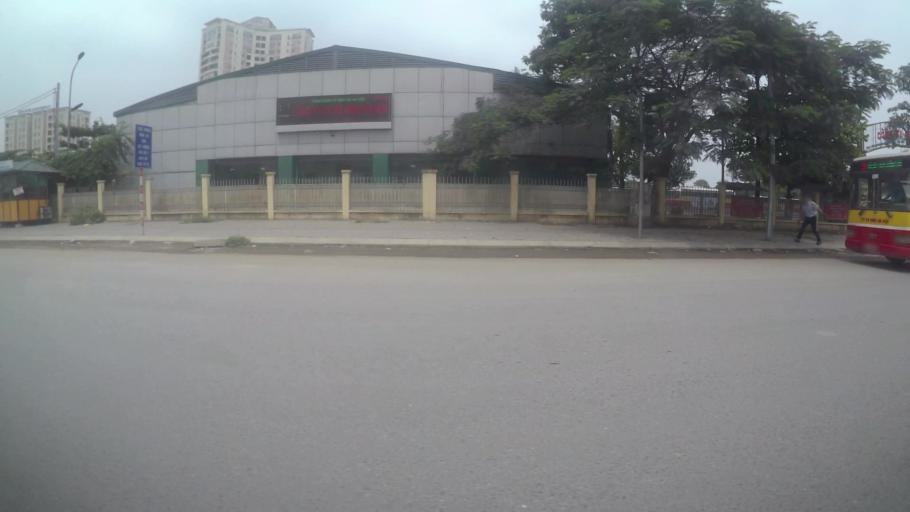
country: VN
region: Ha Noi
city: Tay Ho
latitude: 21.0686
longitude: 105.7851
